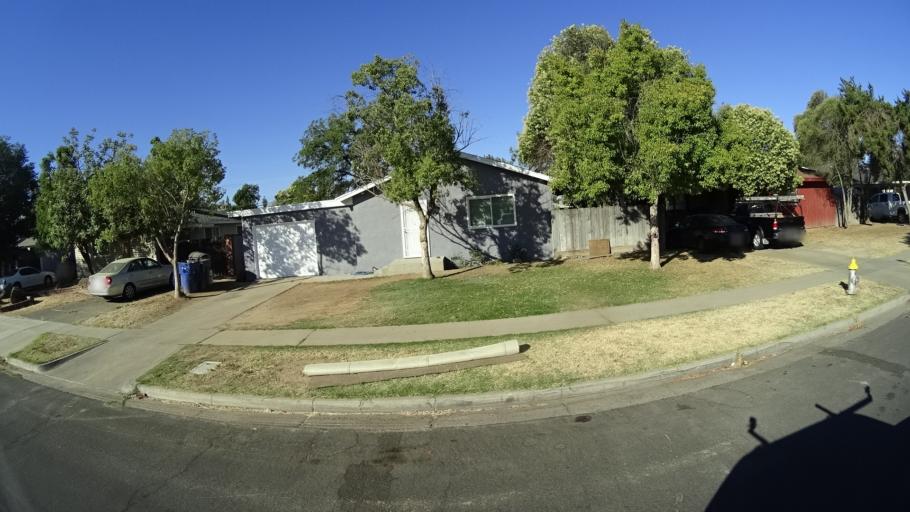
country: US
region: California
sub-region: Fresno County
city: Fresno
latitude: 36.7952
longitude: -119.8226
